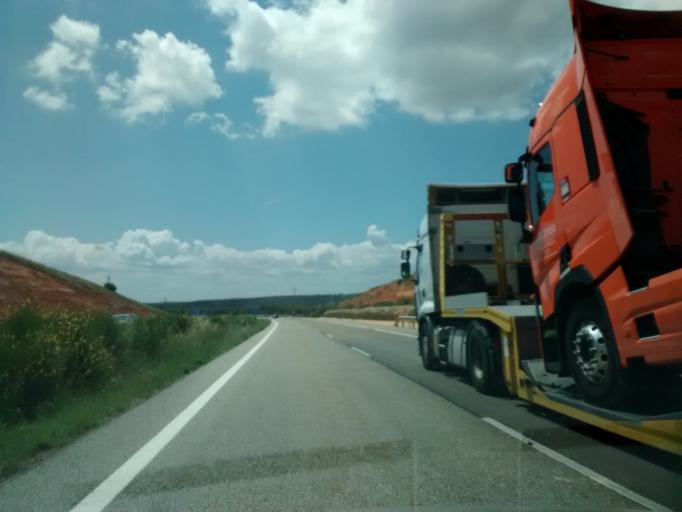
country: ES
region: Castille and Leon
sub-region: Provincia de Leon
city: Astorga
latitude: 42.4640
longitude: -6.0832
